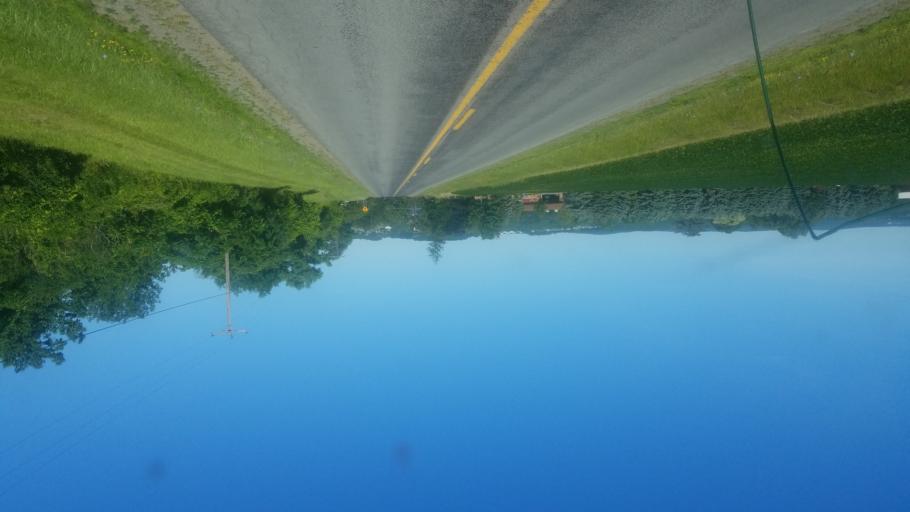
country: US
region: New York
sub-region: Ontario County
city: Canandaigua
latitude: 42.8397
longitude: -77.2522
